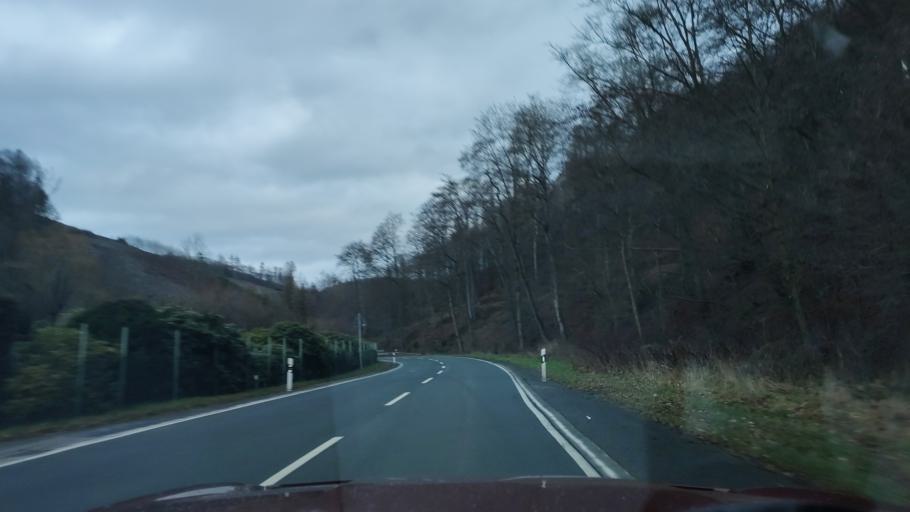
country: DE
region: North Rhine-Westphalia
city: Iserlohn
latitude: 51.3437
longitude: 7.6758
